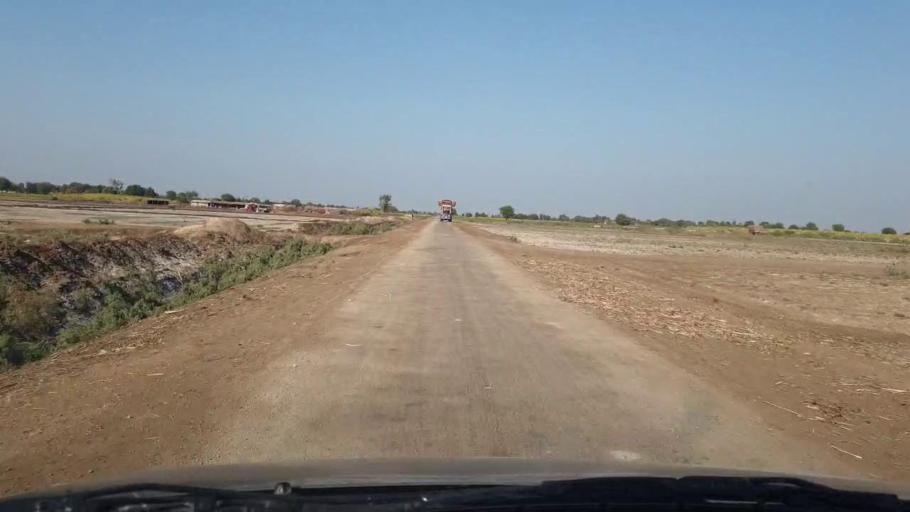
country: PK
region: Sindh
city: Digri
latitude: 25.1413
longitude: 69.2817
